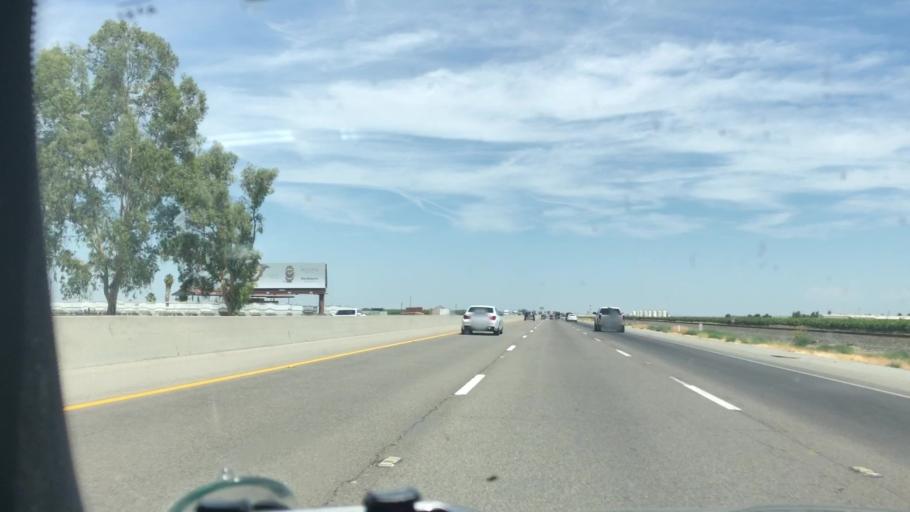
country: US
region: California
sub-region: Kern County
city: McFarland
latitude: 35.6897
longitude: -119.2297
